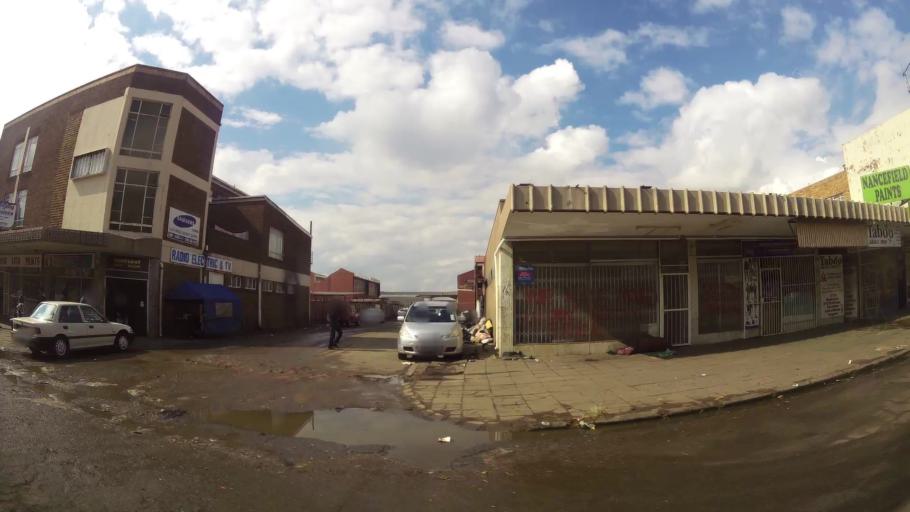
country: ZA
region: Gauteng
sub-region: Sedibeng District Municipality
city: Vereeniging
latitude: -26.6714
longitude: 27.9302
